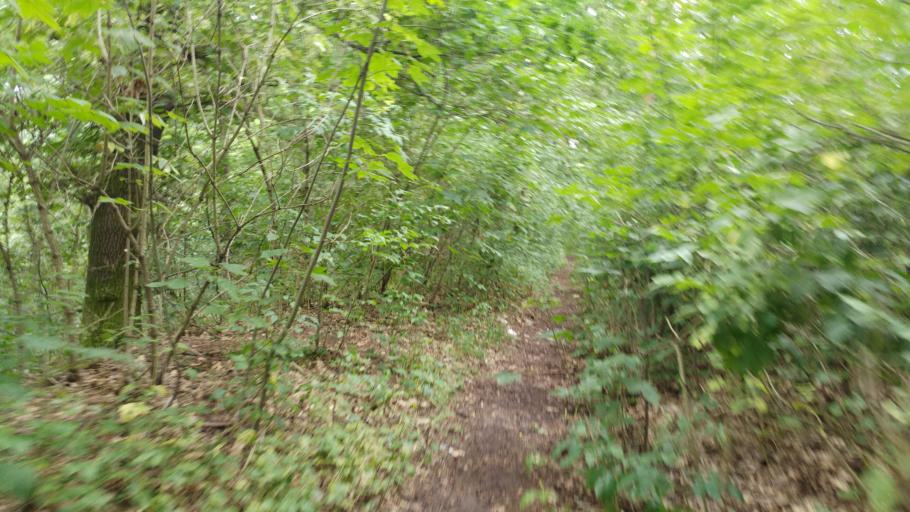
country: CZ
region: Central Bohemia
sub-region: Okres Praha-Zapad
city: Pruhonice
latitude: 50.0364
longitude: 14.5430
